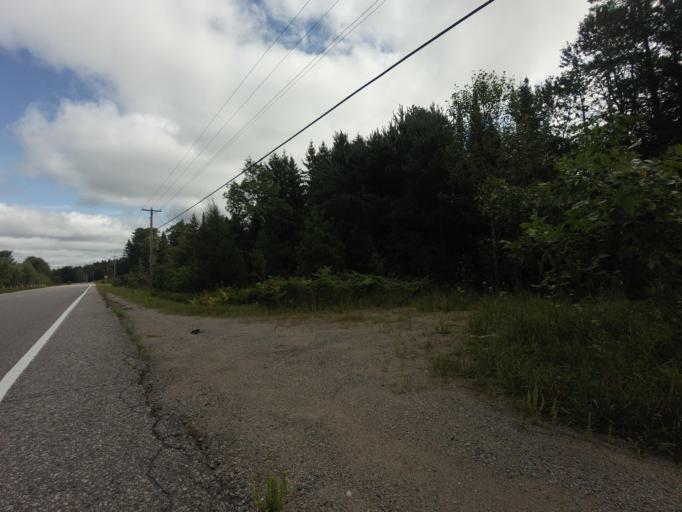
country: CA
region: Ontario
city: Omemee
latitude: 44.8217
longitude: -78.5670
